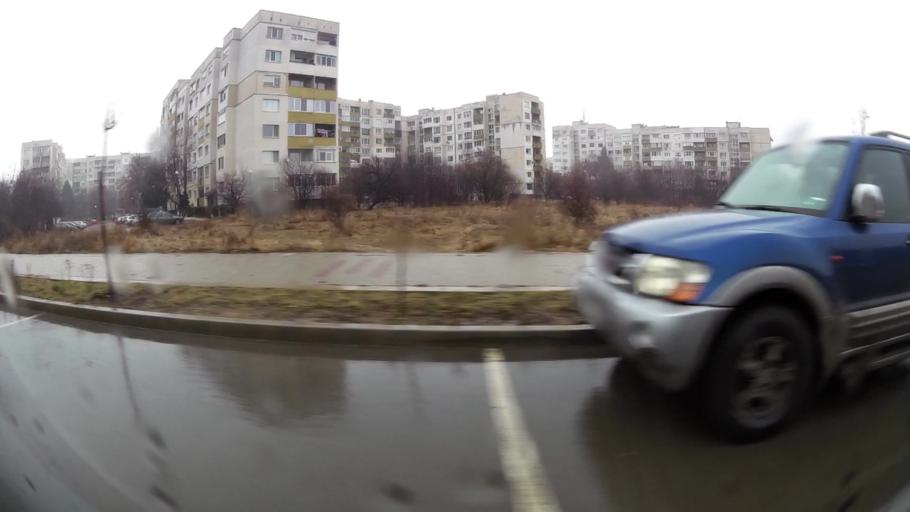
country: BG
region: Sofia-Capital
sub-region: Stolichna Obshtina
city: Sofia
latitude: 42.6519
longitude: 23.3962
